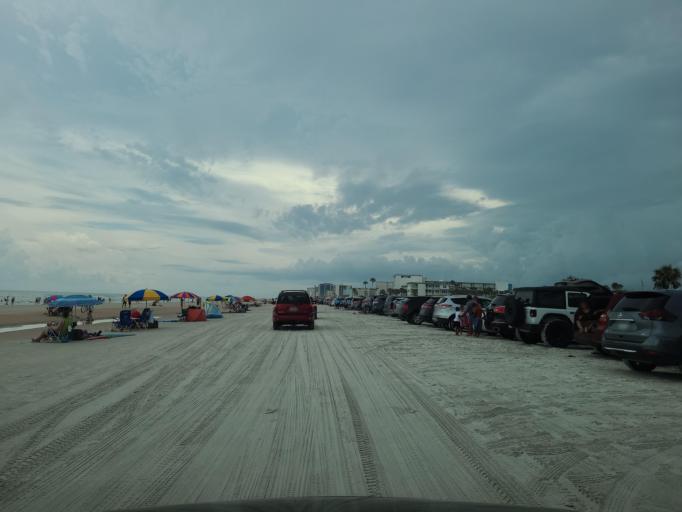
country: US
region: Florida
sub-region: Volusia County
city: Daytona Beach
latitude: 29.2167
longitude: -81.0017
